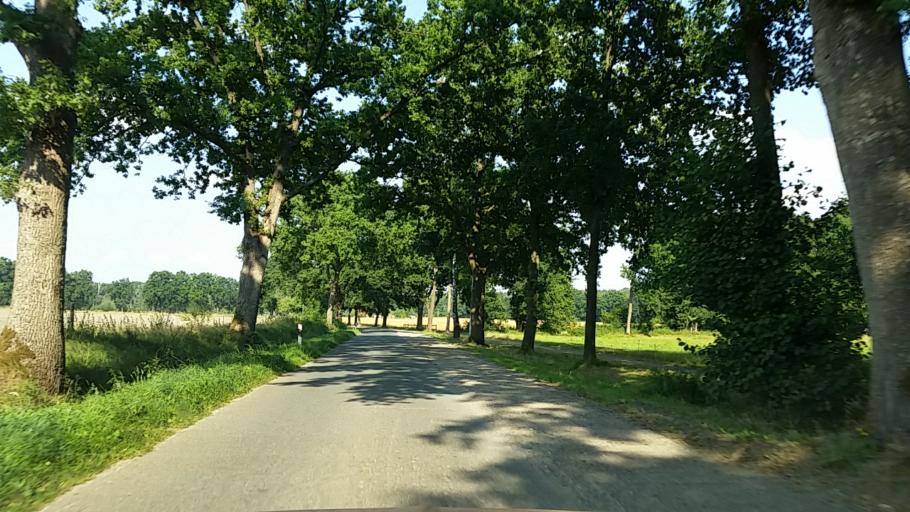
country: DE
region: Lower Saxony
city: Buchholz in der Nordheide
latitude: 53.2812
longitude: 9.9039
